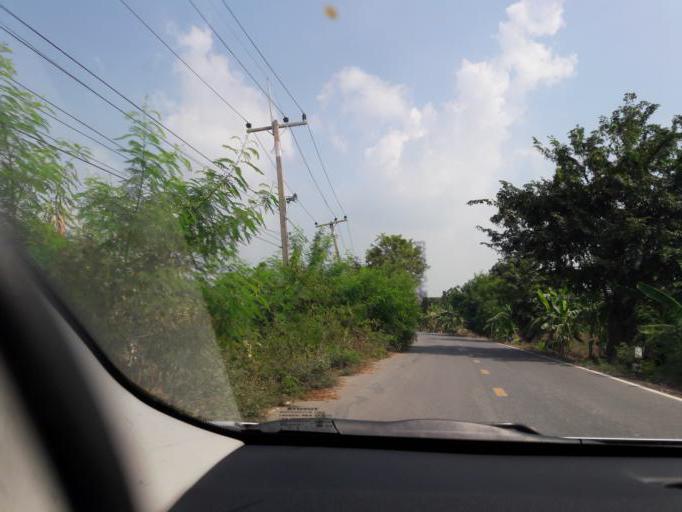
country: TH
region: Ang Thong
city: Ang Thong
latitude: 14.5438
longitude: 100.4145
